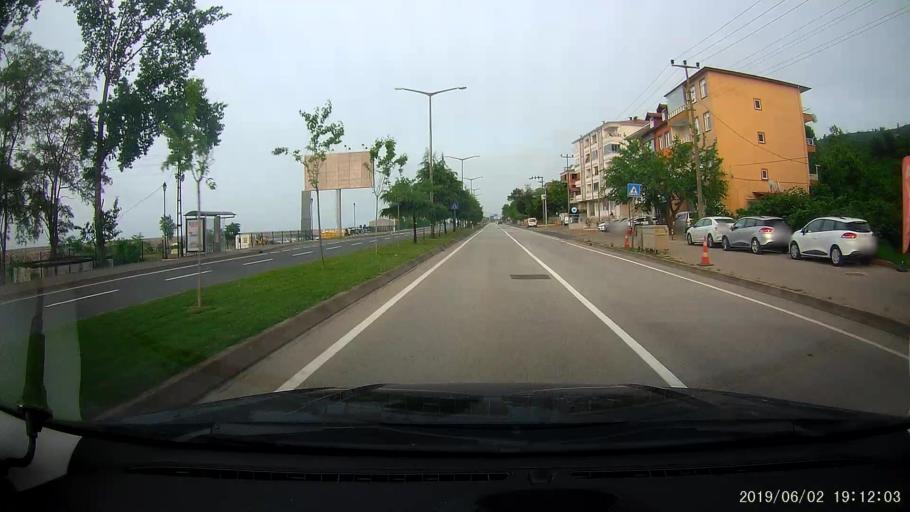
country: TR
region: Ordu
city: Gulyali
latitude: 40.9663
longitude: 38.0623
